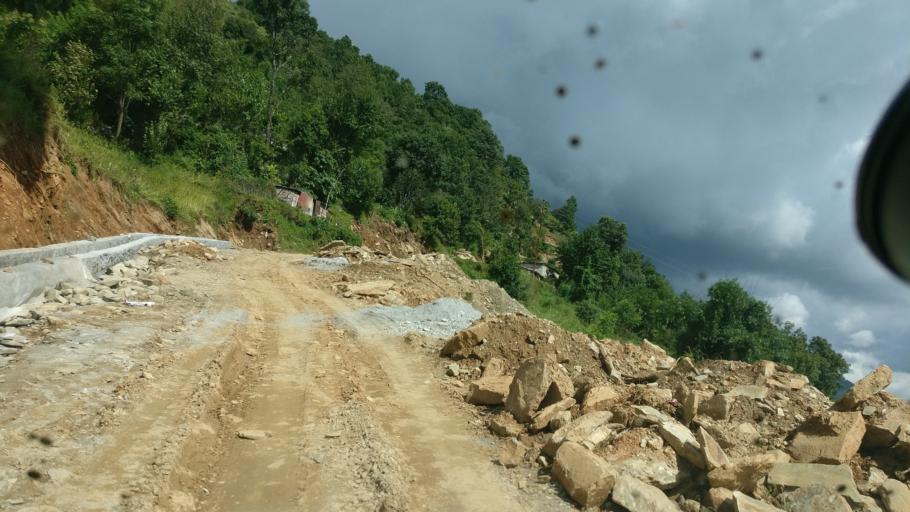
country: NP
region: Western Region
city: Baglung
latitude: 28.2642
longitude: 83.6400
